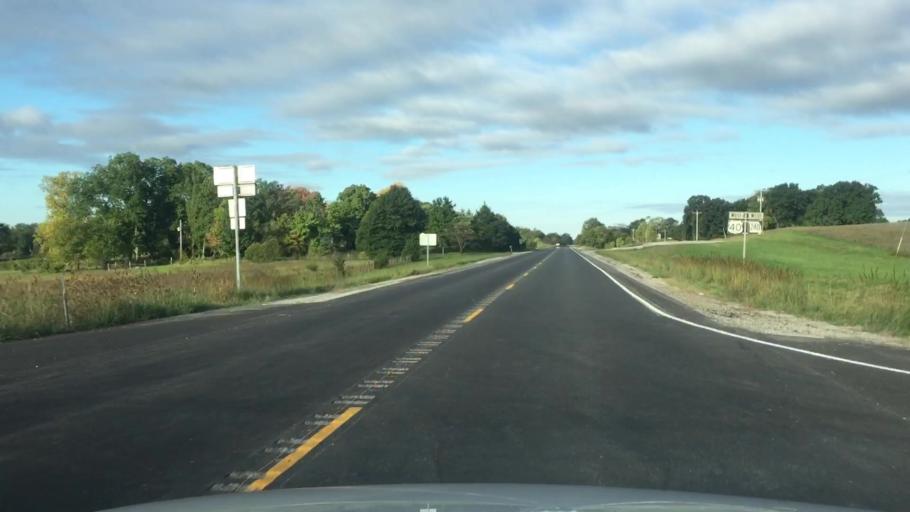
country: US
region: Missouri
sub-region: Boone County
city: Columbia
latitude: 38.9892
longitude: -92.4951
